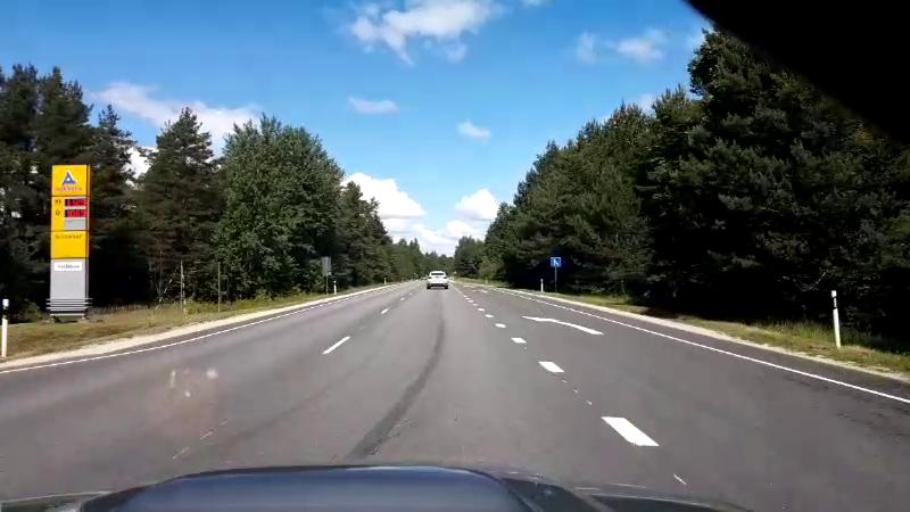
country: EE
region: Paernumaa
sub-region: Paernu linn
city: Parnu
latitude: 58.2137
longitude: 24.4862
